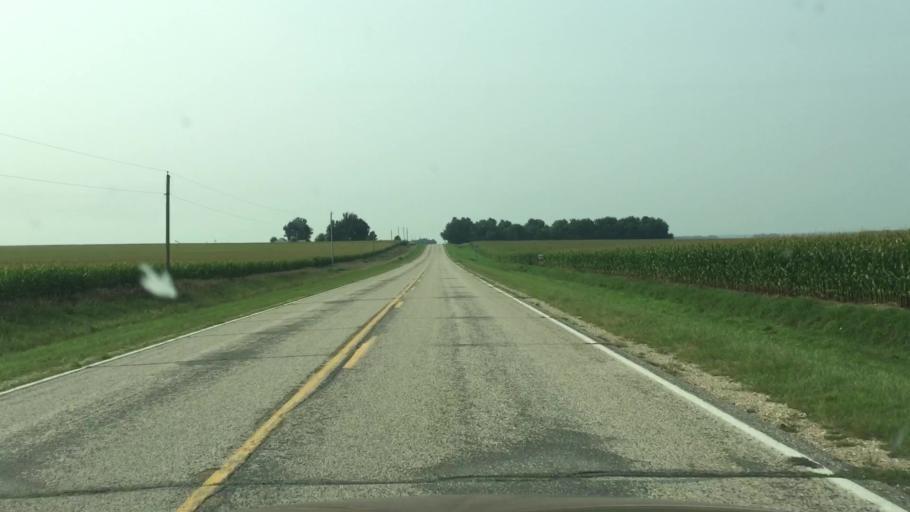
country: US
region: Iowa
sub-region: O'Brien County
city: Sheldon
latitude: 43.2686
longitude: -95.7830
